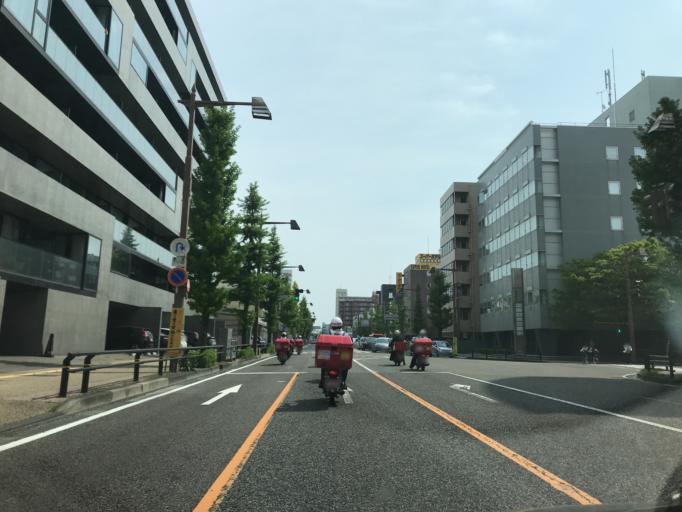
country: JP
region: Niigata
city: Niigata-shi
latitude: 37.9166
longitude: 139.0644
